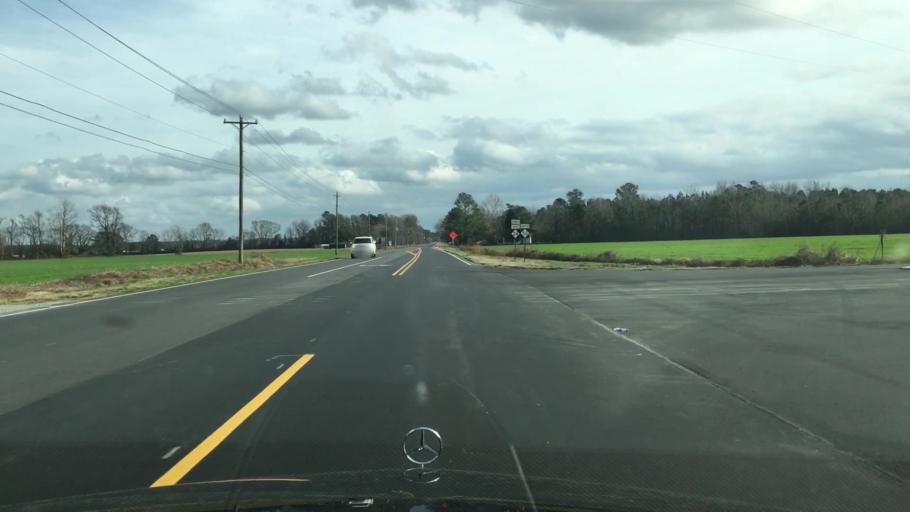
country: US
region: North Carolina
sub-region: Duplin County
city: Warsaw
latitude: 34.9838
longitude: -78.0393
